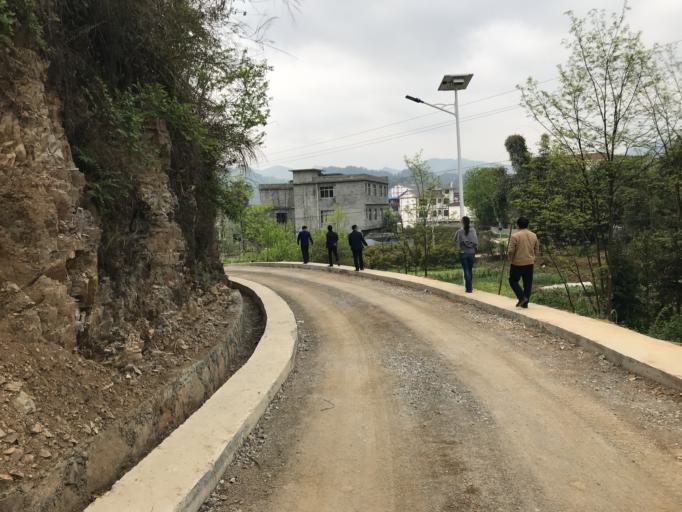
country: CN
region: Guizhou Sheng
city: Longquan
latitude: 28.2026
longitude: 108.0538
